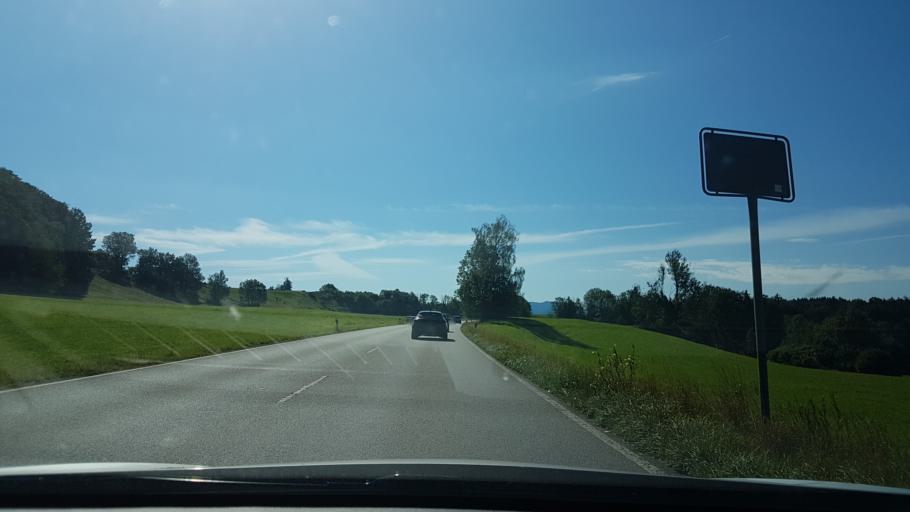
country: DE
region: Bavaria
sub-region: Upper Bavaria
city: Weyarn
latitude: 47.8352
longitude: 11.8199
